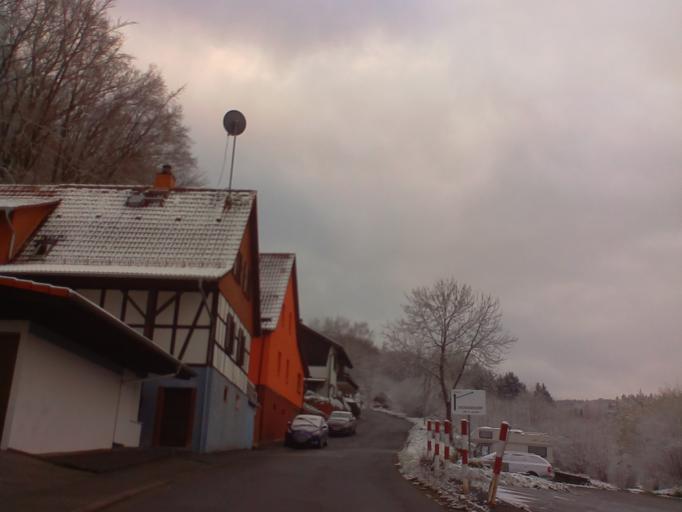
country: DE
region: Hesse
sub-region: Regierungsbezirk Darmstadt
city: Wald-Michelbach
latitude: 49.5620
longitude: 8.8291
